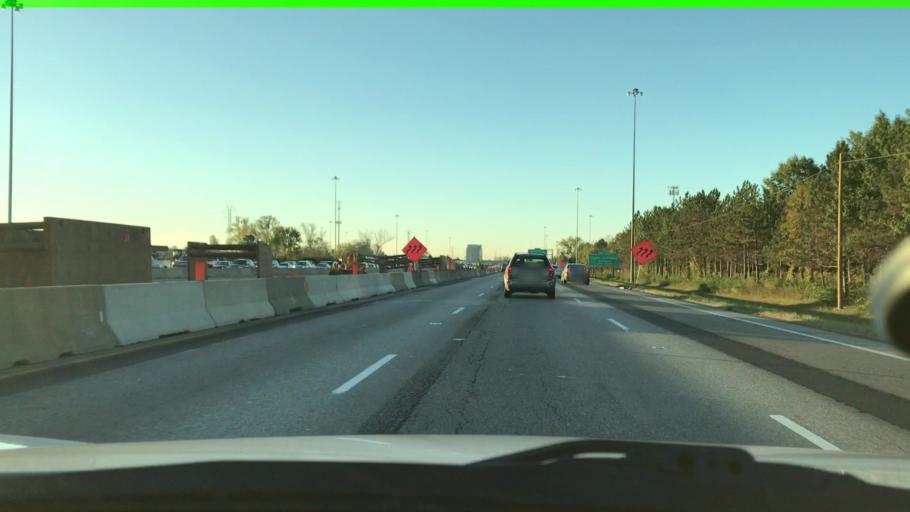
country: US
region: Ohio
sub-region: Franklin County
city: Hilliard
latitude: 40.0404
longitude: -83.1260
